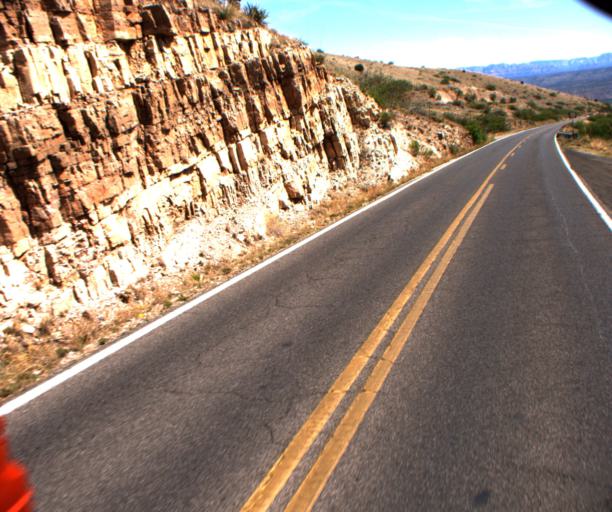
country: US
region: Arizona
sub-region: Yavapai County
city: Clarkdale
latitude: 34.7513
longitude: -112.0982
